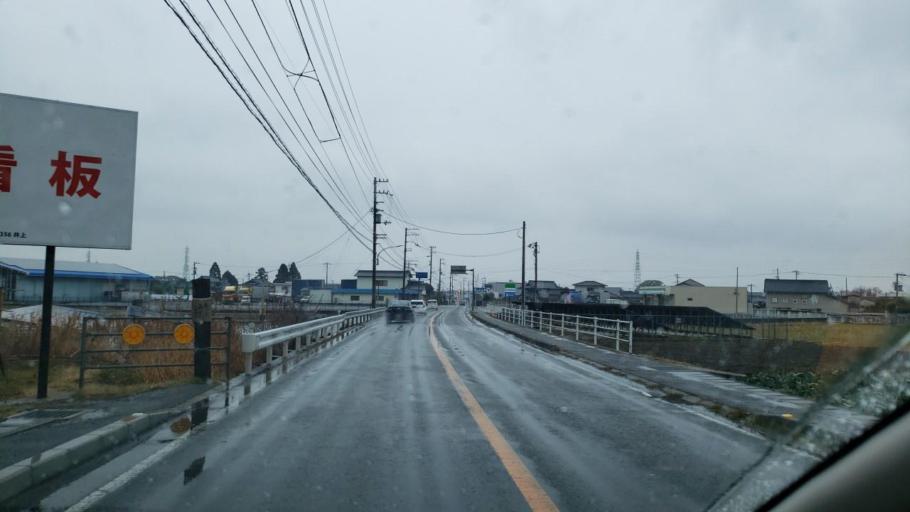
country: JP
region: Tokushima
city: Narutocho-mitsuishi
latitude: 34.1622
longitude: 134.5450
